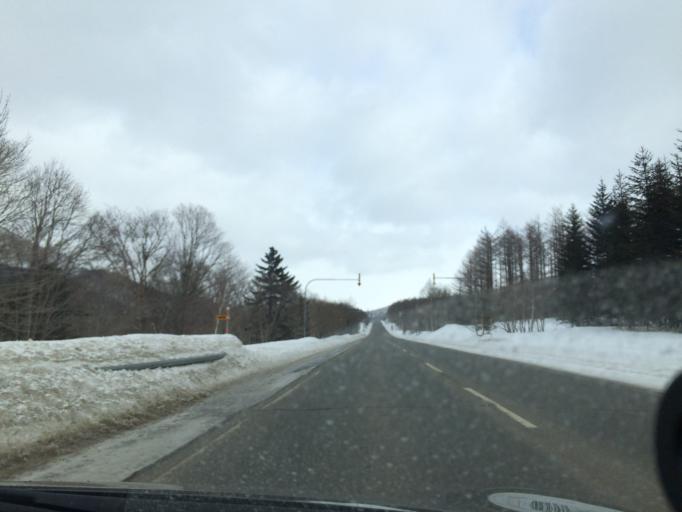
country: JP
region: Hokkaido
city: Shimo-furano
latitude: 43.1318
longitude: 142.7073
